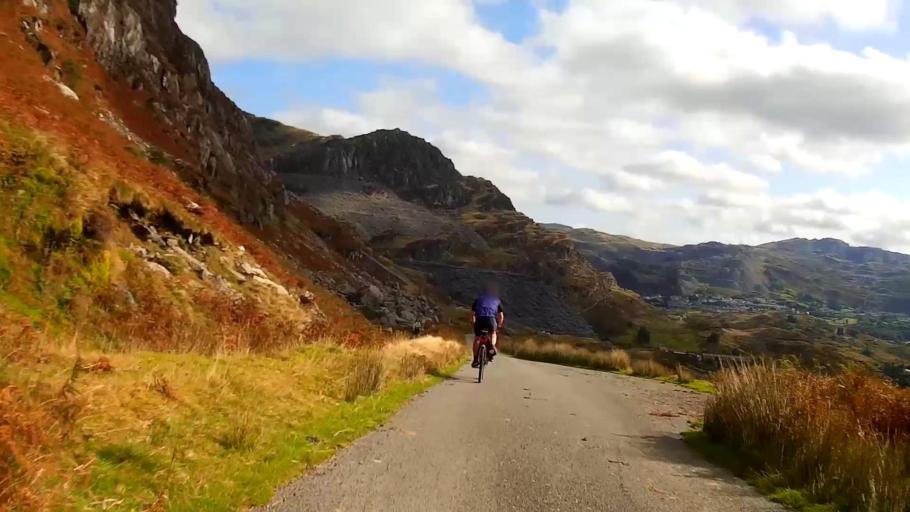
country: GB
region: Wales
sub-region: Gwynedd
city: Blaenau-Ffestiniog
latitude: 52.9865
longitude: -3.9733
